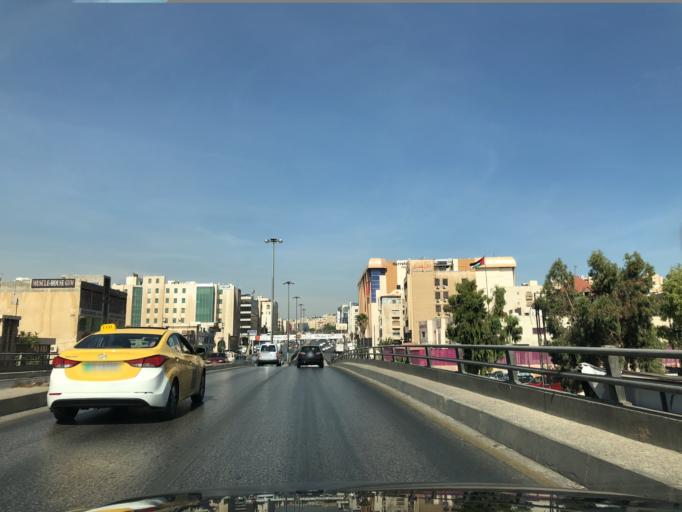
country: JO
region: Amman
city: Al Jubayhah
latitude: 31.9858
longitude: 35.8979
